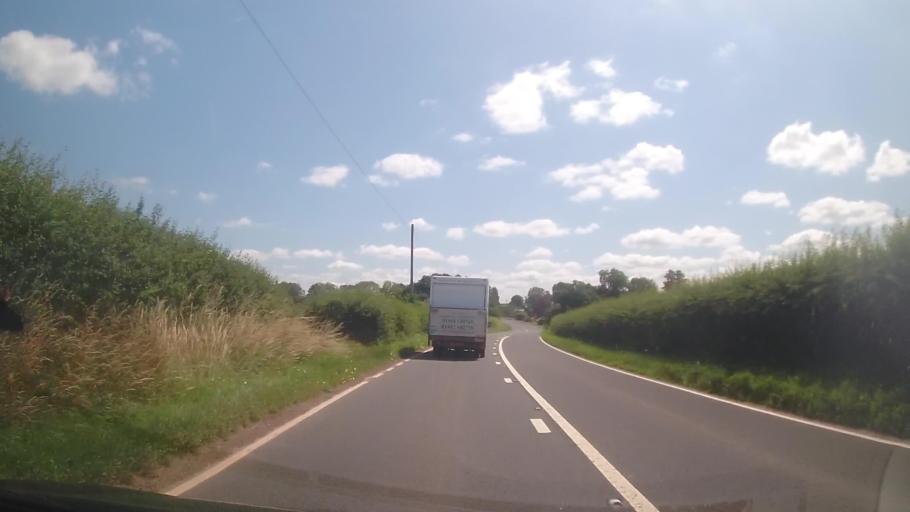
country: GB
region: England
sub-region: Herefordshire
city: Ocle Pychard
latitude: 52.1451
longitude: -2.6266
